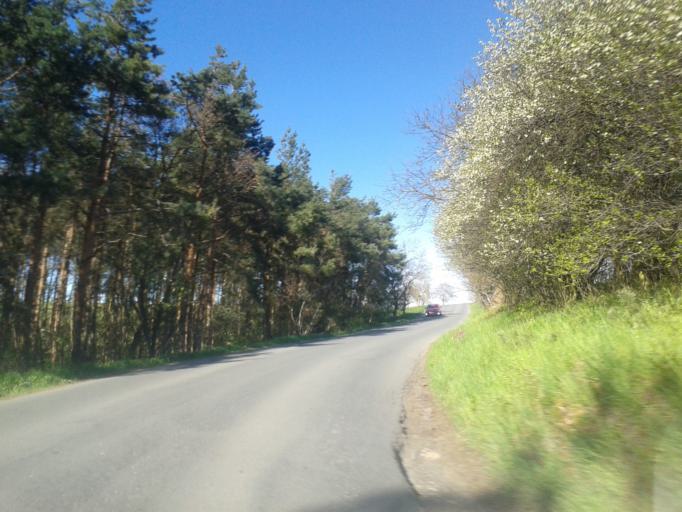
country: CZ
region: Central Bohemia
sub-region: Okres Beroun
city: Beroun
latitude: 49.9279
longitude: 14.0713
